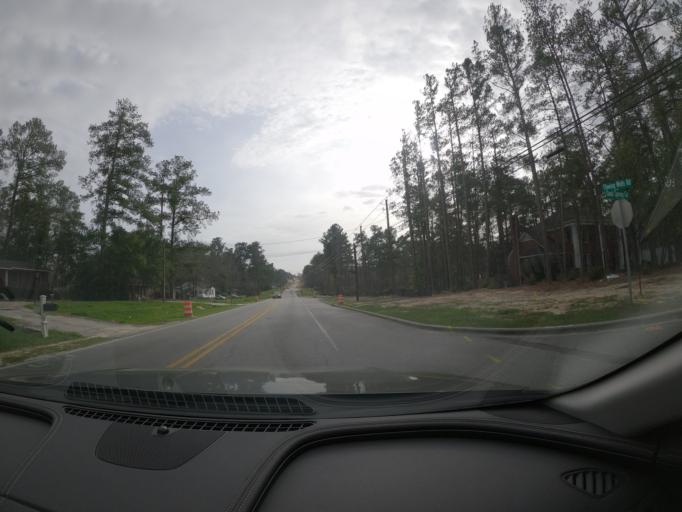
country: US
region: Georgia
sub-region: Columbia County
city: Martinez
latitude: 33.5026
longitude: -82.1070
